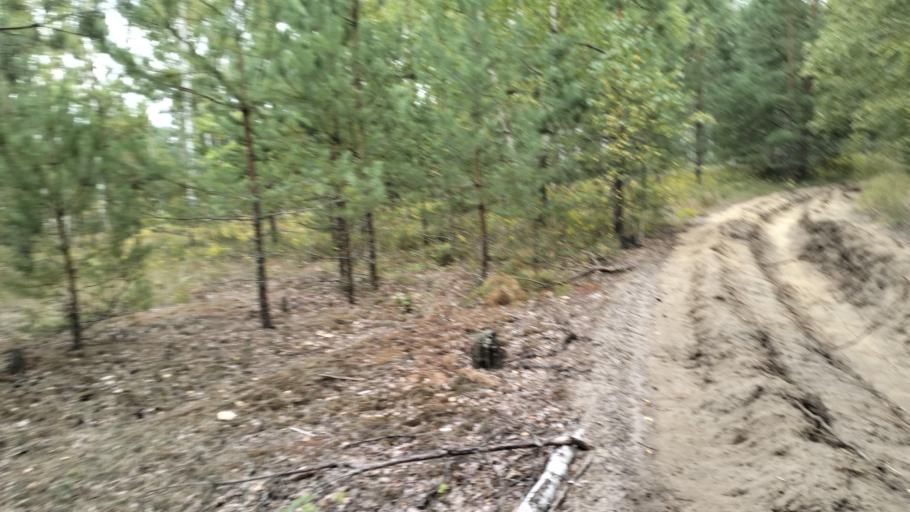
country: BY
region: Brest
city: Davyd-Haradok
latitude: 51.8755
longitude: 27.2099
